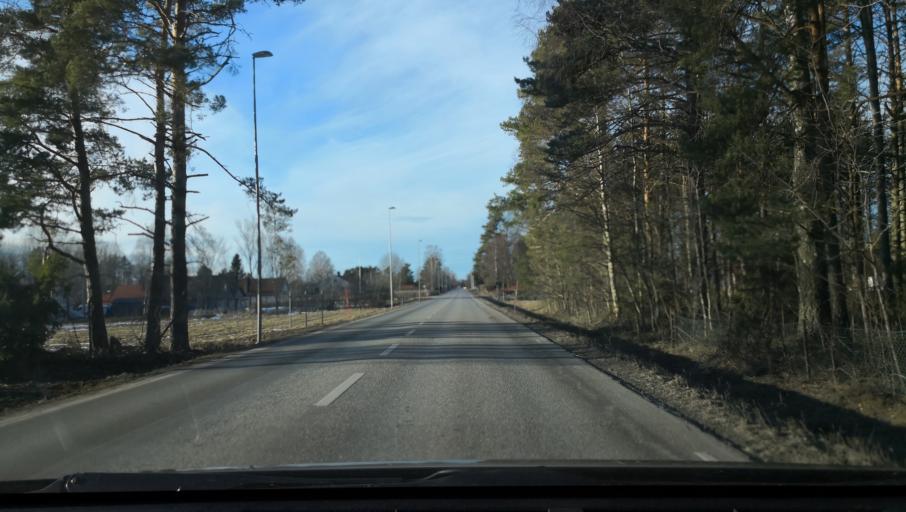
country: SE
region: Uppsala
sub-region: Osthammars Kommun
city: OEsthammar
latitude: 60.2811
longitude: 18.2963
